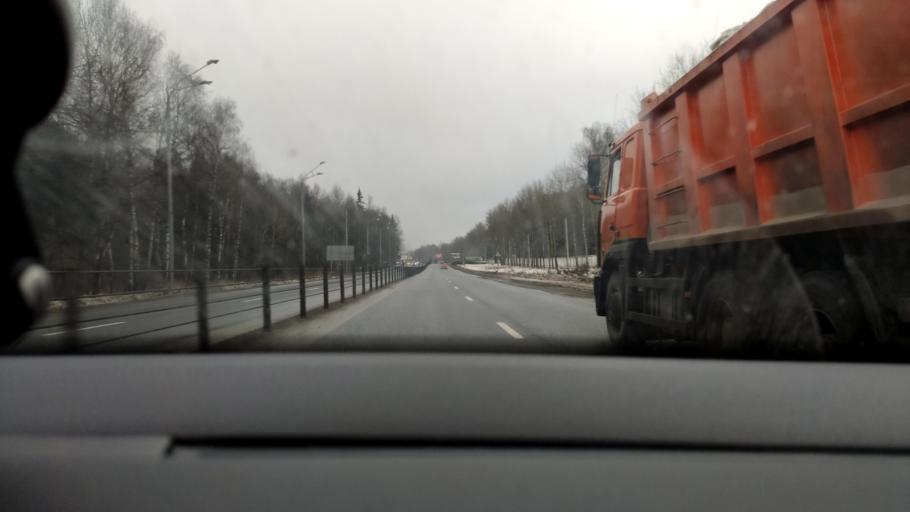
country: RU
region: Moskovskaya
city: Sergiyev Posad
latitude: 56.2572
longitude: 38.1265
